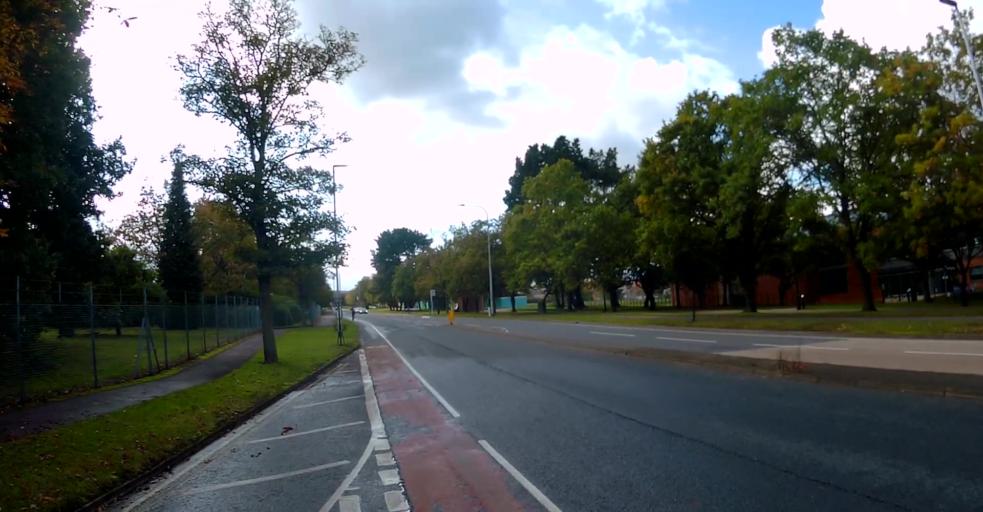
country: GB
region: England
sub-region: Hampshire
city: Aldershot
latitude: 51.2592
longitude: -0.7613
